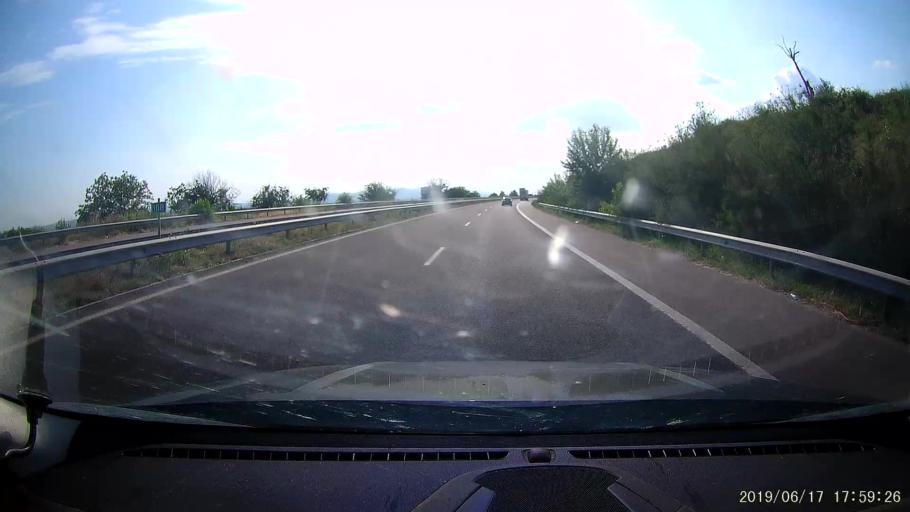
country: BG
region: Khaskovo
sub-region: Obshtina Svilengrad
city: Svilengrad
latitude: 41.7245
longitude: 26.2978
